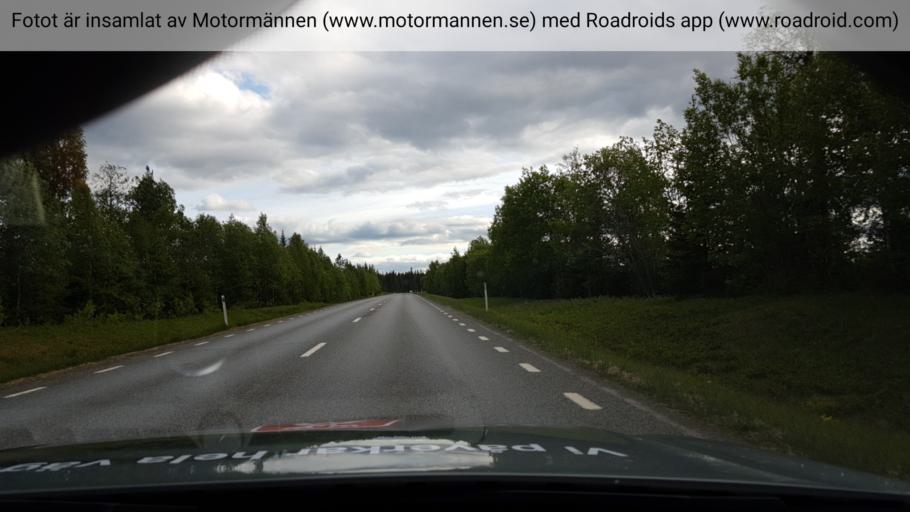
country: SE
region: Jaemtland
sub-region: Stroemsunds Kommun
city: Stroemsund
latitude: 63.5132
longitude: 15.2871
